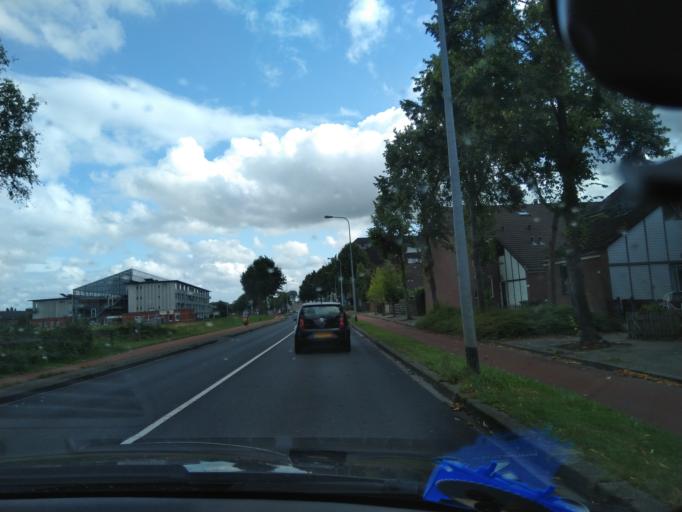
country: NL
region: Groningen
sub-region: Gemeente Groningen
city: Groningen
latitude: 53.2062
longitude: 6.5078
